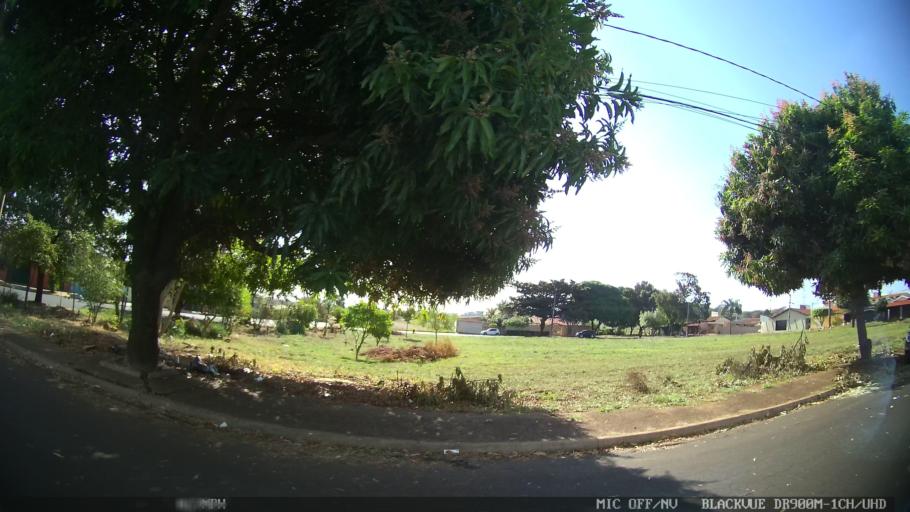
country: BR
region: Sao Paulo
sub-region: Ribeirao Preto
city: Ribeirao Preto
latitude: -21.1771
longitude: -47.7764
